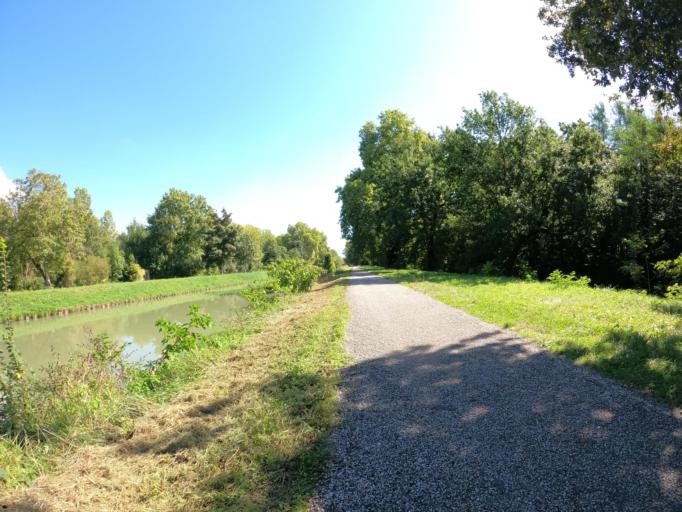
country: FR
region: Midi-Pyrenees
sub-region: Departement du Tarn-et-Garonne
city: Valence
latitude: 44.1079
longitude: 0.8811
